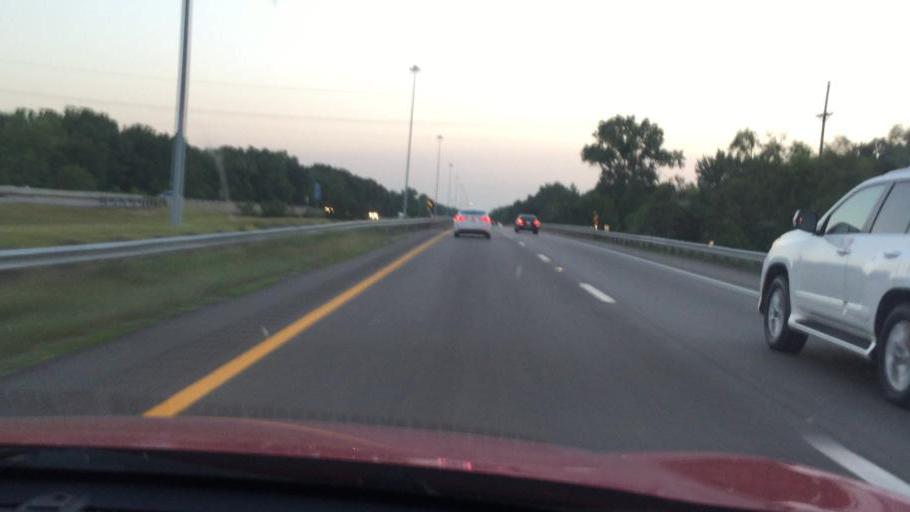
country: US
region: Ohio
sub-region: Lucas County
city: Holland
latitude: 41.6379
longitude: -83.6943
